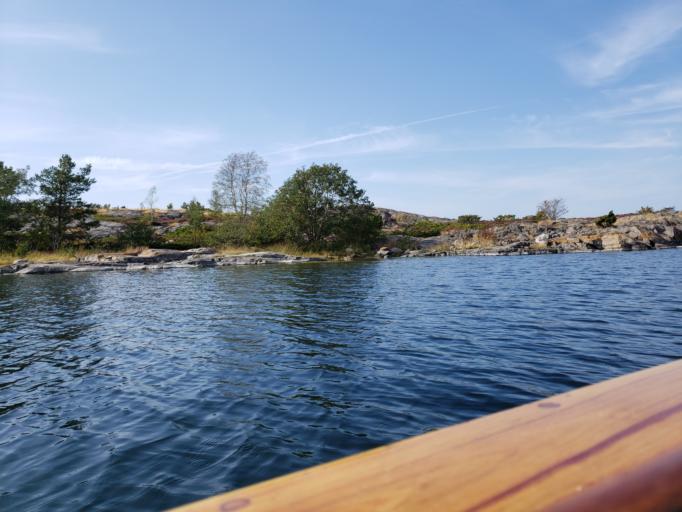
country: FI
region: Varsinais-Suomi
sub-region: Aboland-Turunmaa
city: Dragsfjaerd
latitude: 59.8445
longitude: 22.2063
